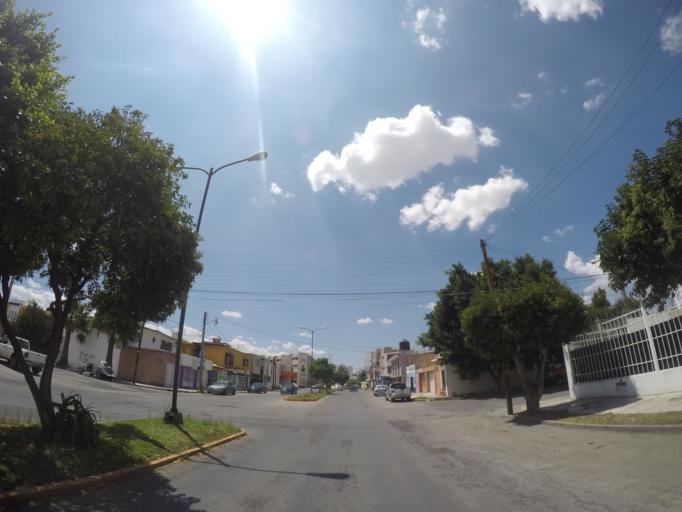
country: MX
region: San Luis Potosi
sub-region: San Luis Potosi
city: San Luis Potosi
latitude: 22.1441
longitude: -100.9886
